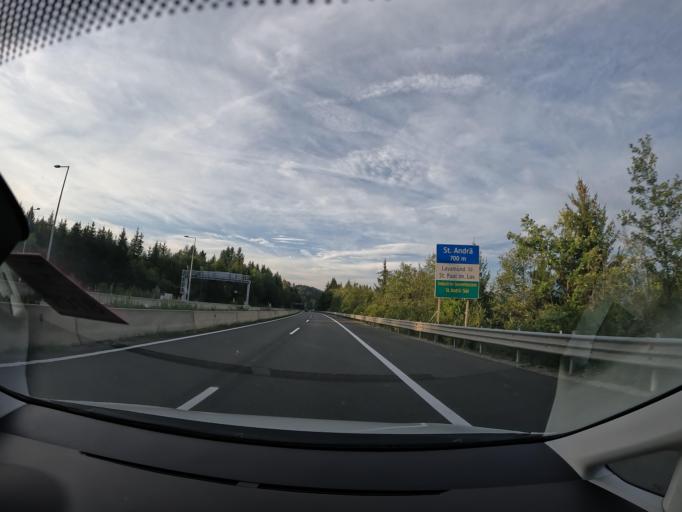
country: AT
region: Carinthia
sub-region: Politischer Bezirk Wolfsberg
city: Sankt Andrae
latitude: 46.7361
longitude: 14.8050
